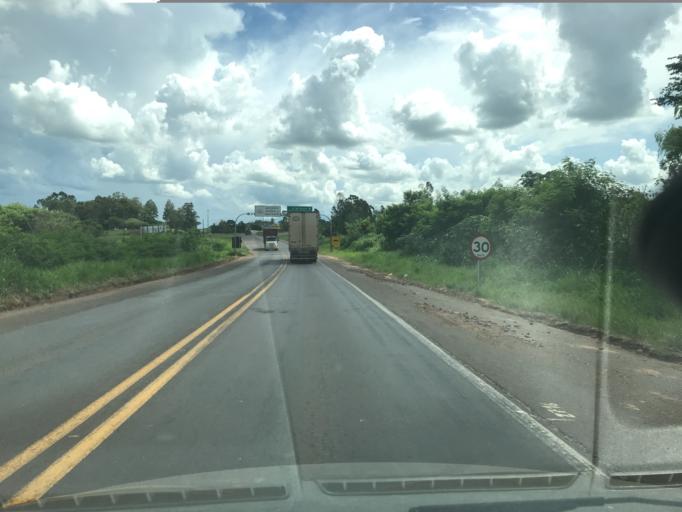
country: BR
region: Parana
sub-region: Cruzeiro Do Oeste
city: Cruzeiro do Oeste
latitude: -23.7934
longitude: -53.0444
